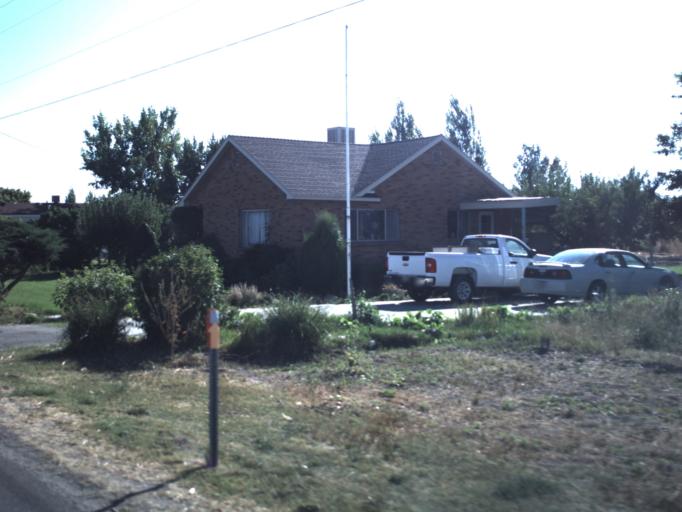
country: US
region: Utah
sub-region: Weber County
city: Hooper
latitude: 41.1738
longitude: -112.1227
